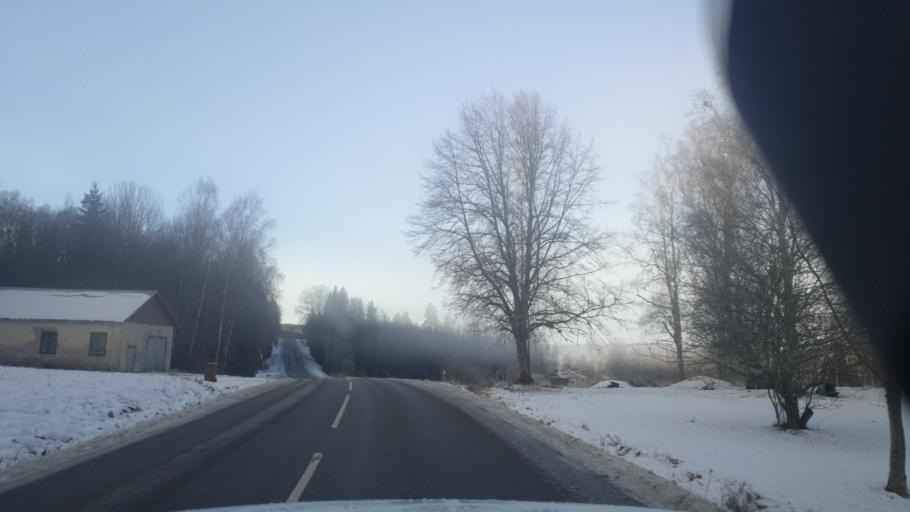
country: SE
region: Vaermland
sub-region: Arvika Kommun
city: Arvika
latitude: 59.6529
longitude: 12.4554
